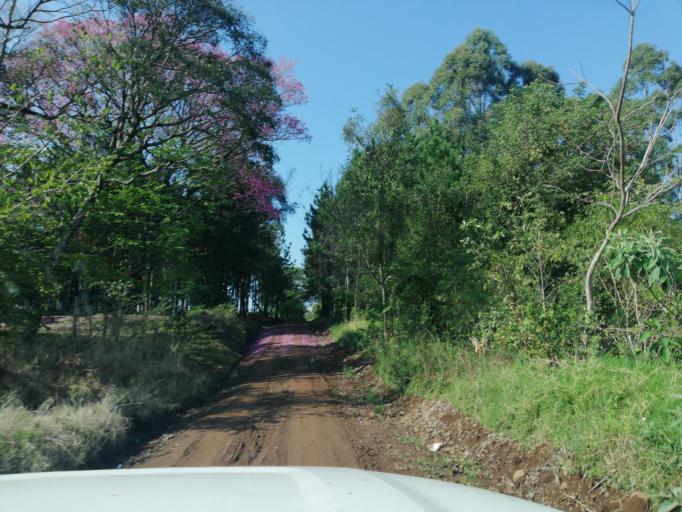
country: AR
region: Misiones
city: Cerro Azul
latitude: -27.6258
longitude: -55.5245
